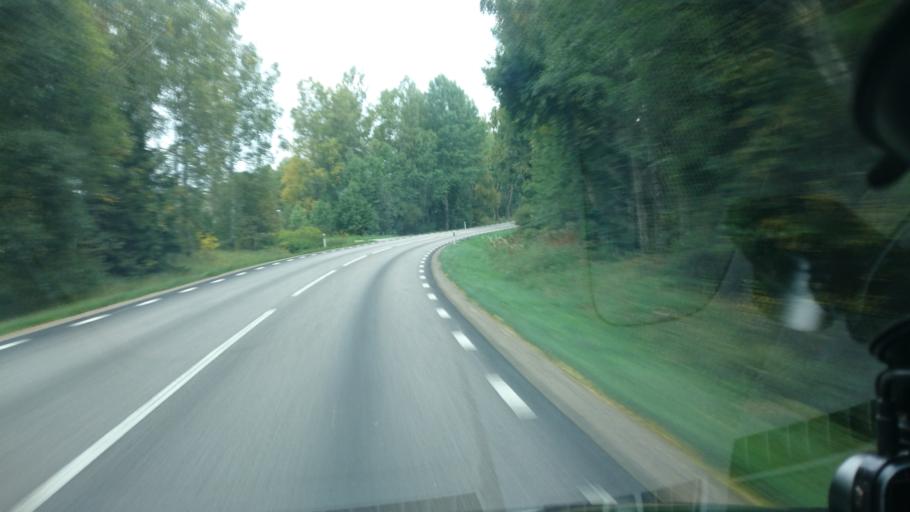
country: SE
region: Vaestra Goetaland
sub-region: Svenljunga Kommun
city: Svenljunga
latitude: 57.5917
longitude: 13.1220
